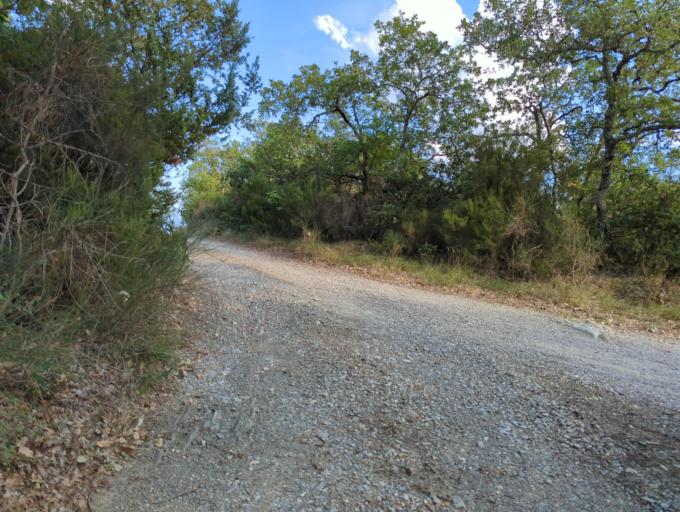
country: IT
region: Tuscany
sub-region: Province of Arezzo
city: Castiglion Fibocchi
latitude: 43.5389
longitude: 11.7879
